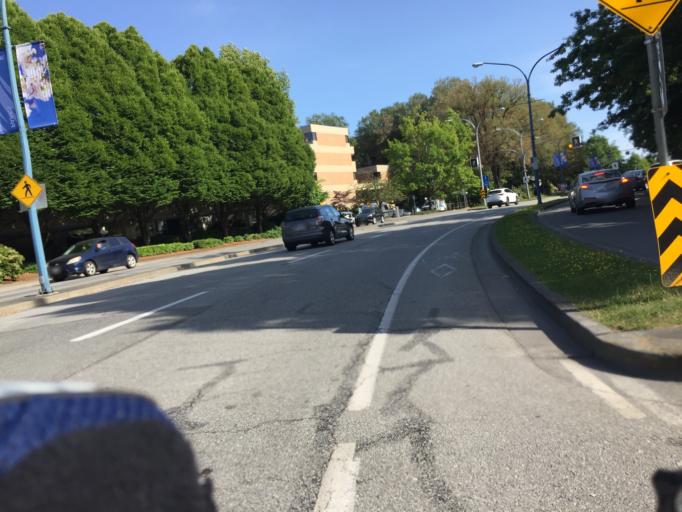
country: CA
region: British Columbia
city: Richmond
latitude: 49.1645
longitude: -123.1405
